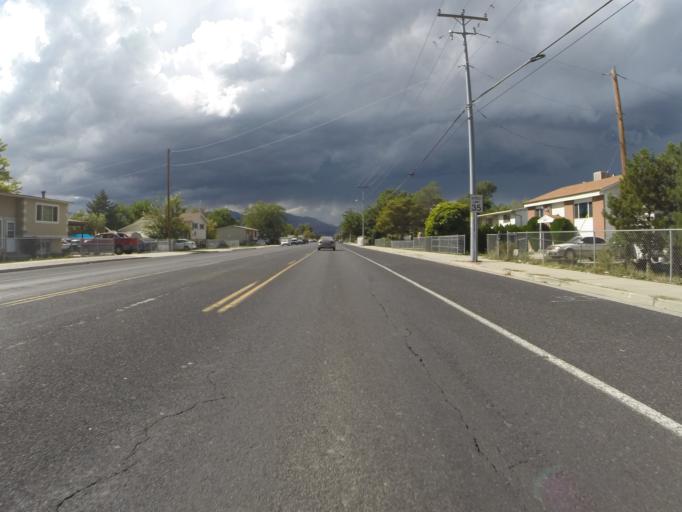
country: US
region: Utah
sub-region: Salt Lake County
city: West Valley City
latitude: 40.7039
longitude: -111.9900
